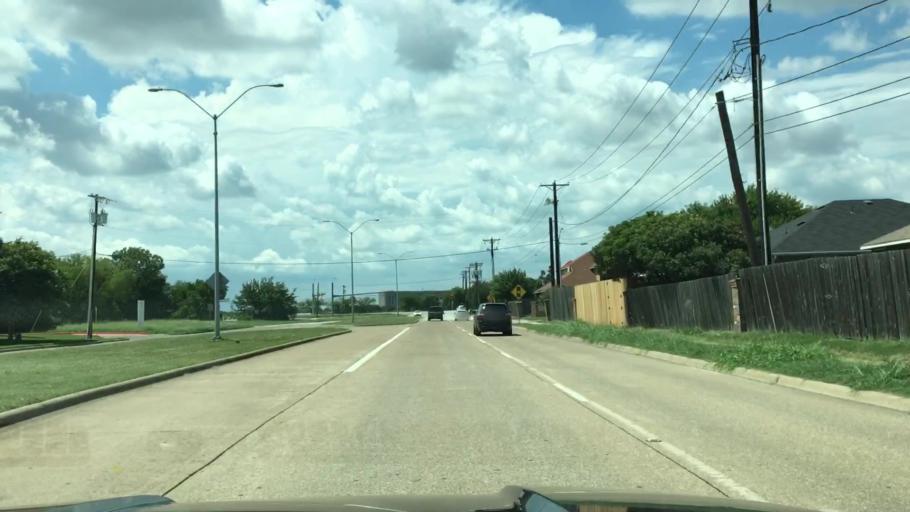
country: US
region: Texas
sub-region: Tarrant County
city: Blue Mound
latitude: 32.8638
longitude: -97.3396
